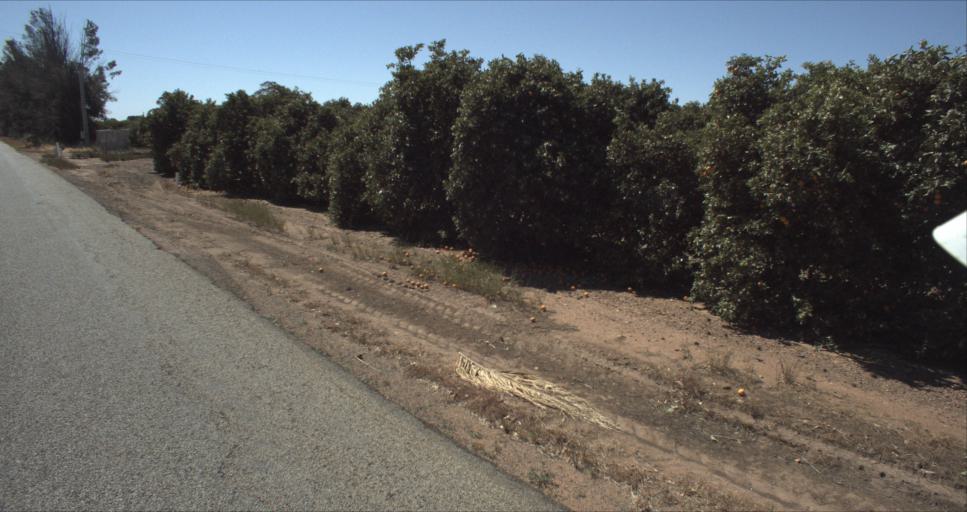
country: AU
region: New South Wales
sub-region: Leeton
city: Leeton
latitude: -34.5367
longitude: 146.3585
